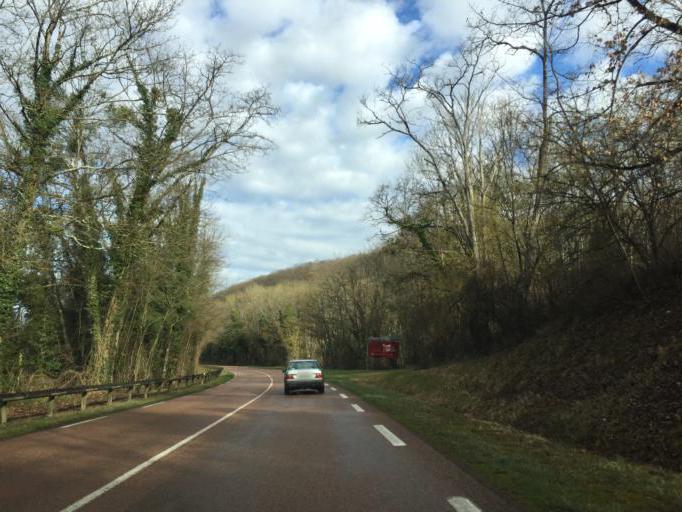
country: FR
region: Bourgogne
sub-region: Departement de la Nievre
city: Clamecy
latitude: 47.4454
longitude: 3.5578
